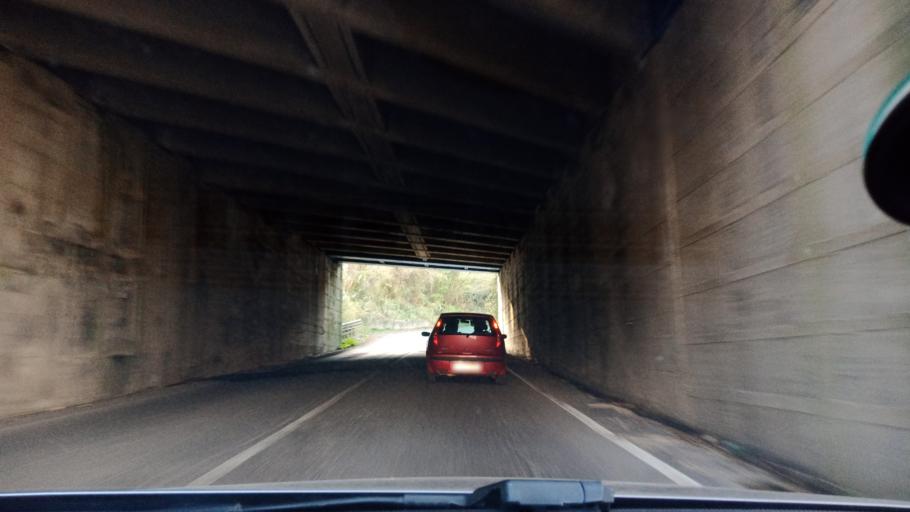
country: IT
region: Latium
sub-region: Citta metropolitana di Roma Capitale
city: Nazzano
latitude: 42.2159
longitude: 12.5982
